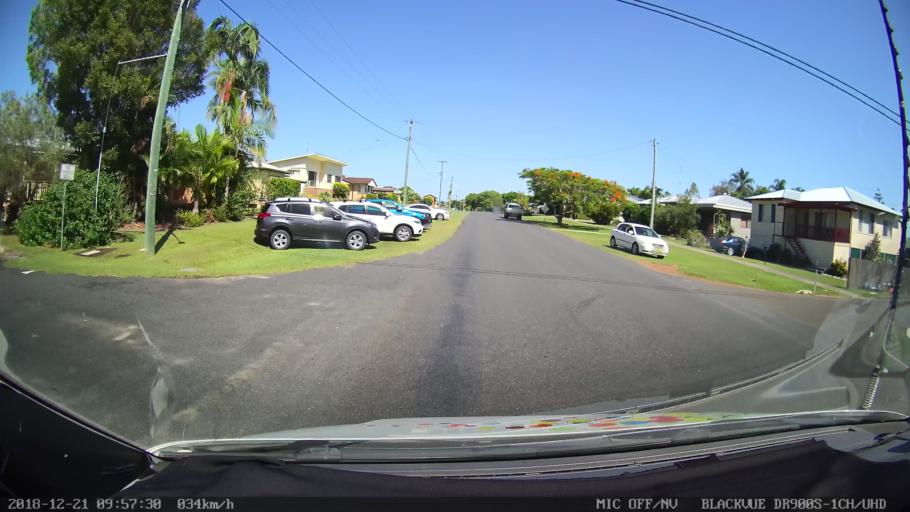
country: AU
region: New South Wales
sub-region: Clarence Valley
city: Grafton
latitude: -29.6745
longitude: 152.9388
